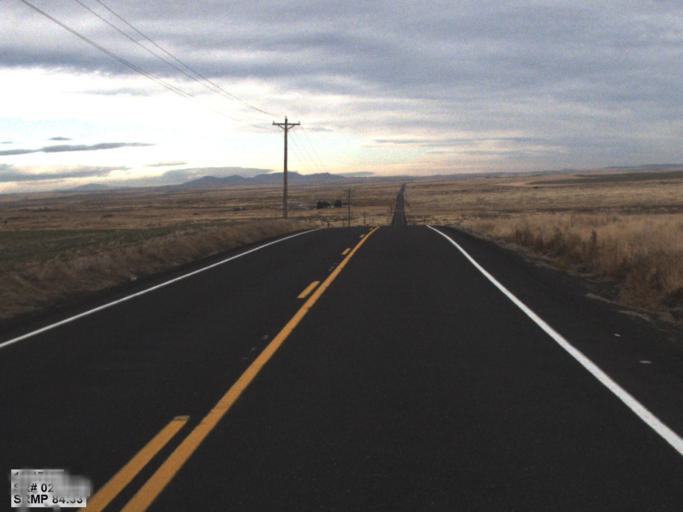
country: US
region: Washington
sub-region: Okanogan County
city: Coulee Dam
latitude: 47.6594
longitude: -118.7214
